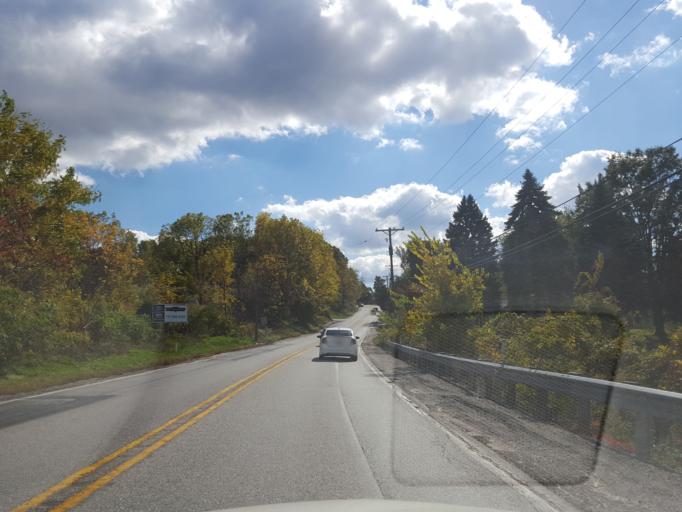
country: US
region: Pennsylvania
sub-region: York County
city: Yoe
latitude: 39.9382
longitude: -76.6442
